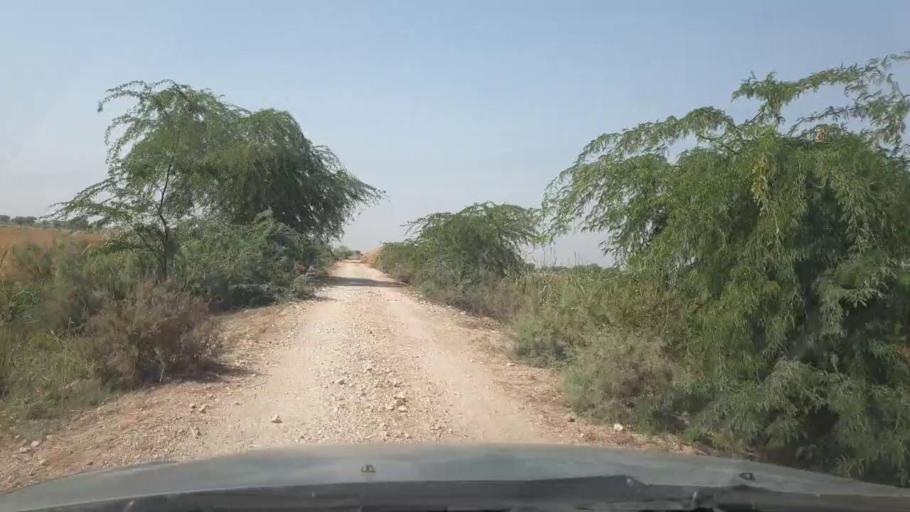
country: PK
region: Sindh
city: Bulri
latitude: 24.8717
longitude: 68.4526
